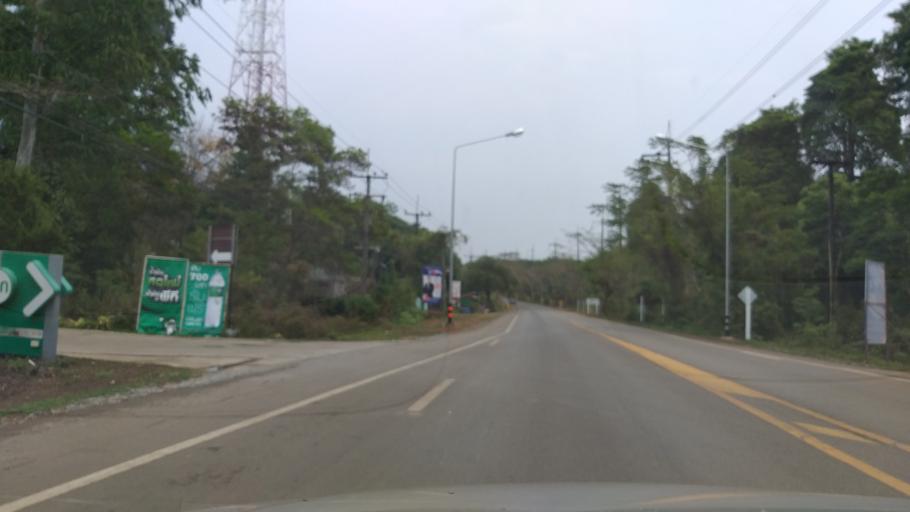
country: TH
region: Trat
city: Laem Ngop
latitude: 12.2592
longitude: 102.2886
